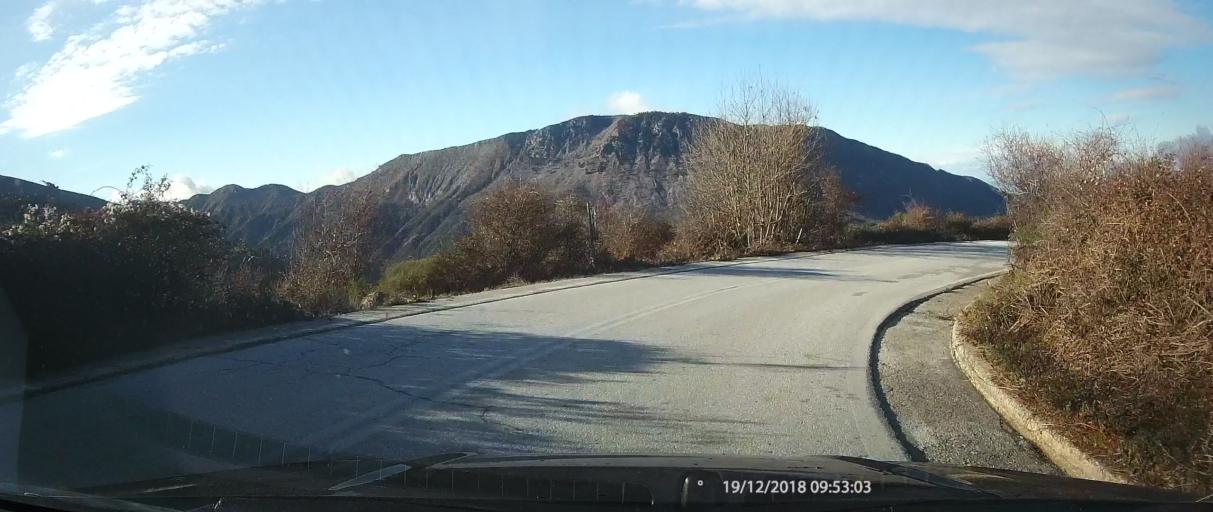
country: GR
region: Peloponnese
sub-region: Nomos Messinias
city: Paralia Vergas
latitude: 37.0700
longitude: 22.2559
